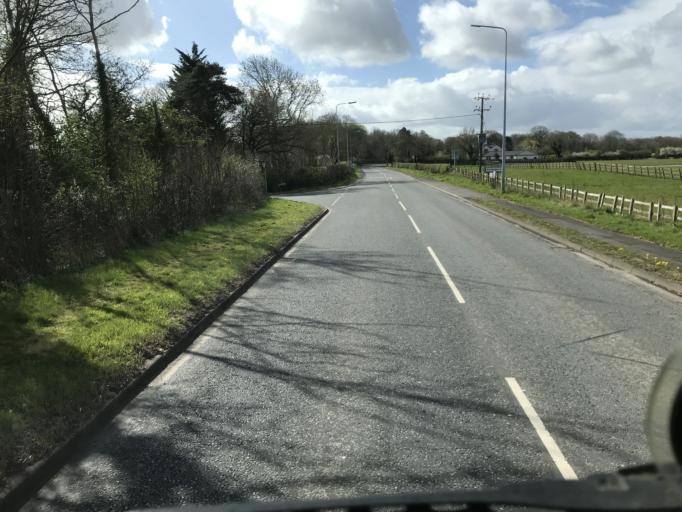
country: GB
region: England
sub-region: Cheshire West and Chester
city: Eccleston
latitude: 53.1498
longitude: -2.9170
